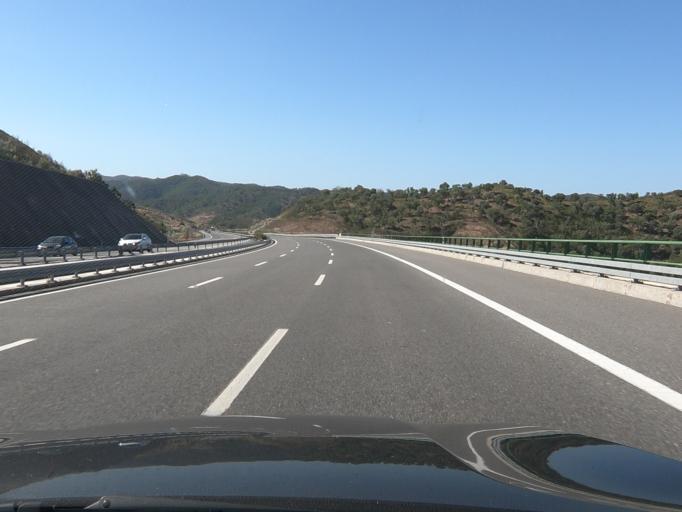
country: PT
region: Faro
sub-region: Silves
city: Sao Bartolomeu de Messines
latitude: 37.4021
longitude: -8.2621
